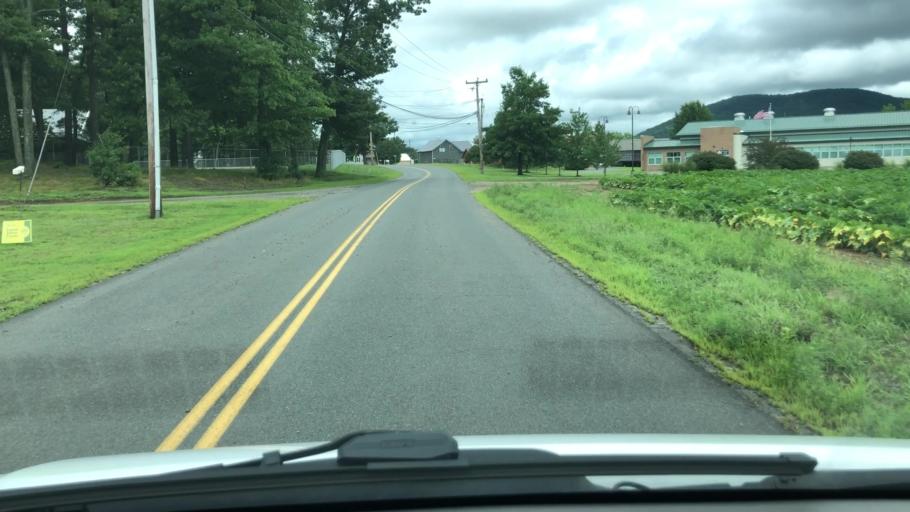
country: US
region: Massachusetts
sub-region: Franklin County
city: South Deerfield
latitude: 42.4603
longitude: -72.6088
